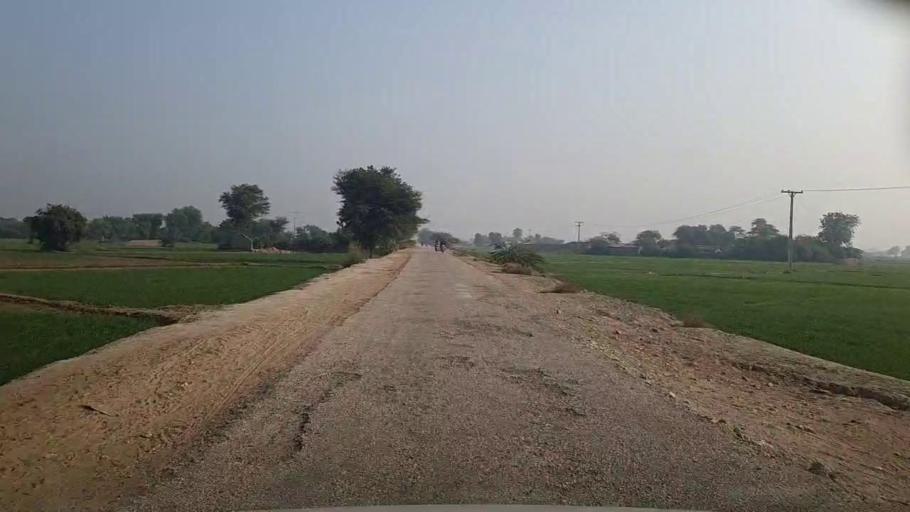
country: PK
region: Sindh
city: Kandiari
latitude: 27.0482
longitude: 68.4695
